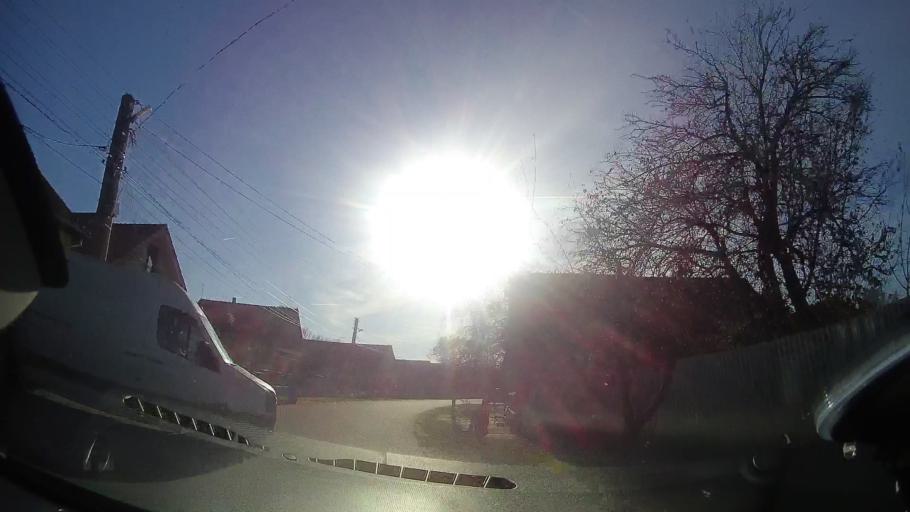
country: RO
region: Bihor
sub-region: Comuna Auseu
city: Grosi
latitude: 47.0256
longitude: 22.4735
